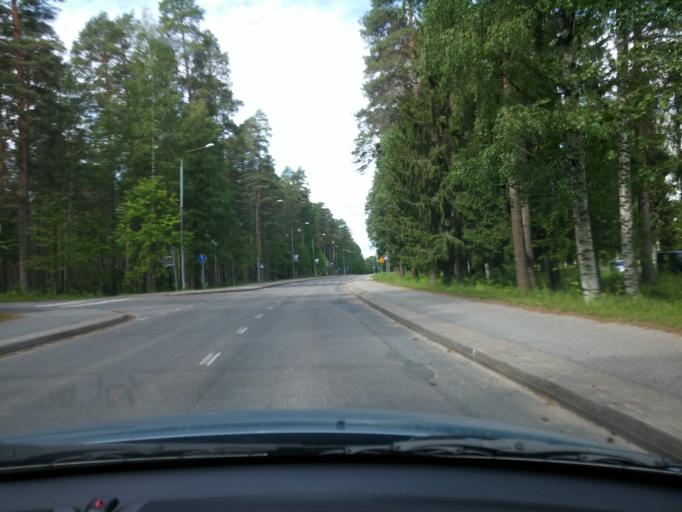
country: FI
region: Central Finland
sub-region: Saarijaervi-Viitasaari
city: Saarijaervi
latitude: 62.7056
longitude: 25.2361
